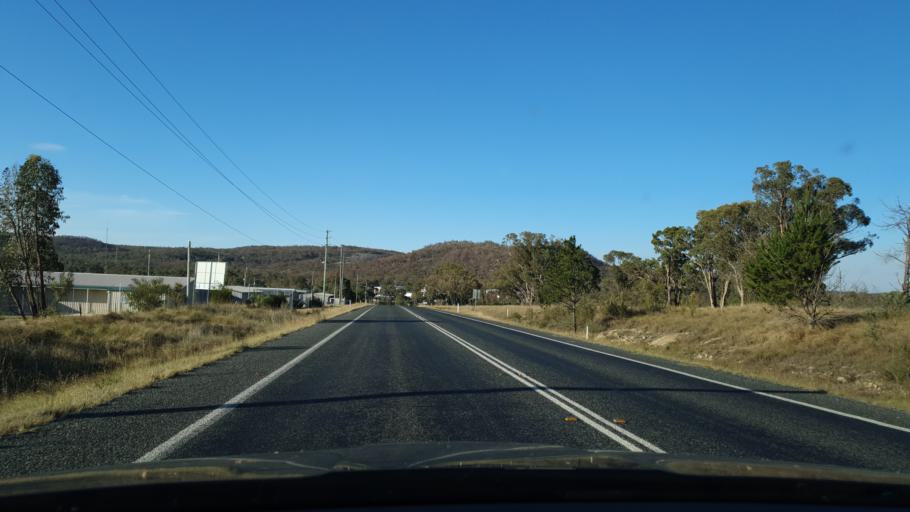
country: AU
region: Queensland
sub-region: Southern Downs
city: Stanthorpe
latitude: -28.6581
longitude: 151.9169
